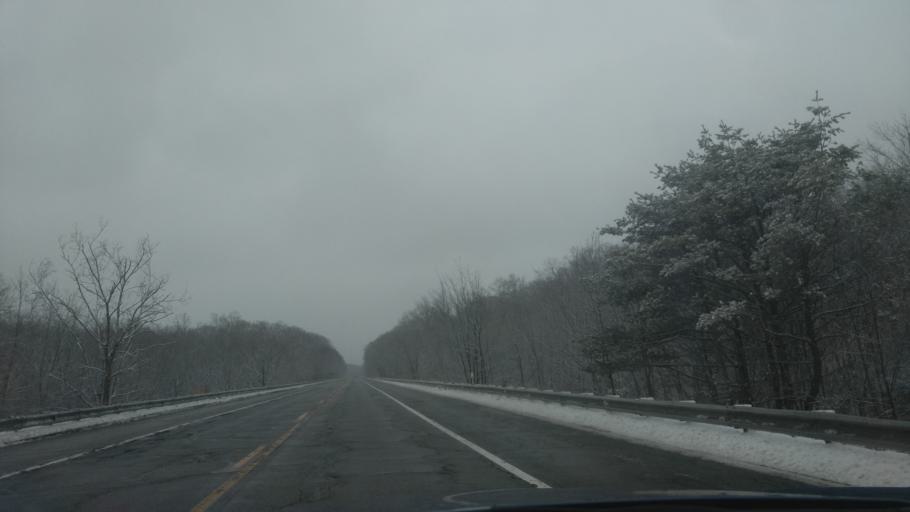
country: US
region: Rhode Island
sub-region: Providence County
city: North Scituate
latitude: 41.8346
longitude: -71.6471
